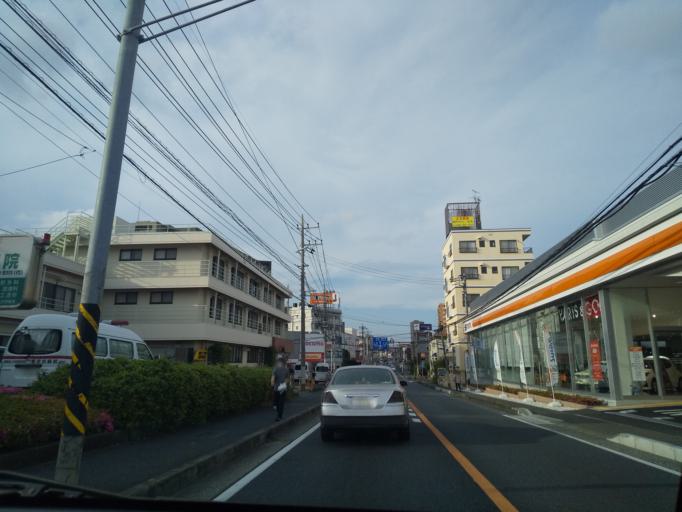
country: JP
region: Kanagawa
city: Zama
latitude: 35.5057
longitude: 139.4121
